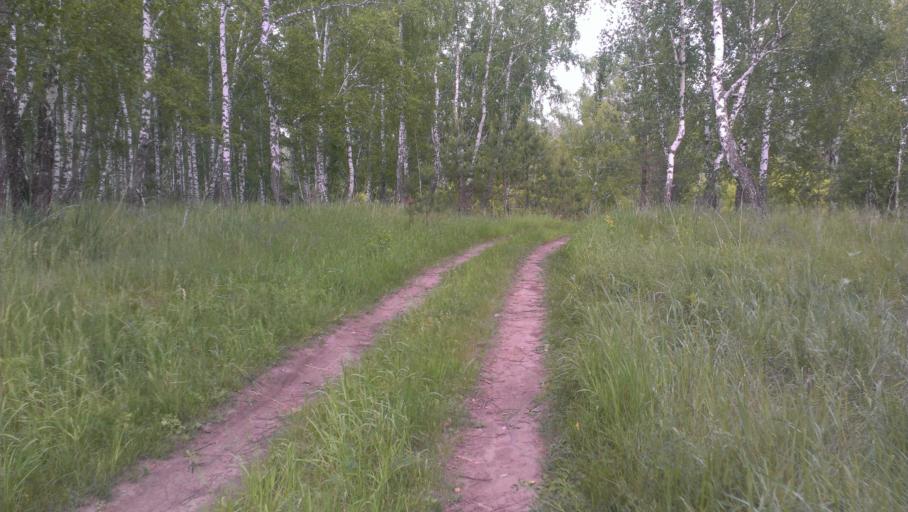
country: RU
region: Altai Krai
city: Sannikovo
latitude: 53.3392
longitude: 84.0570
